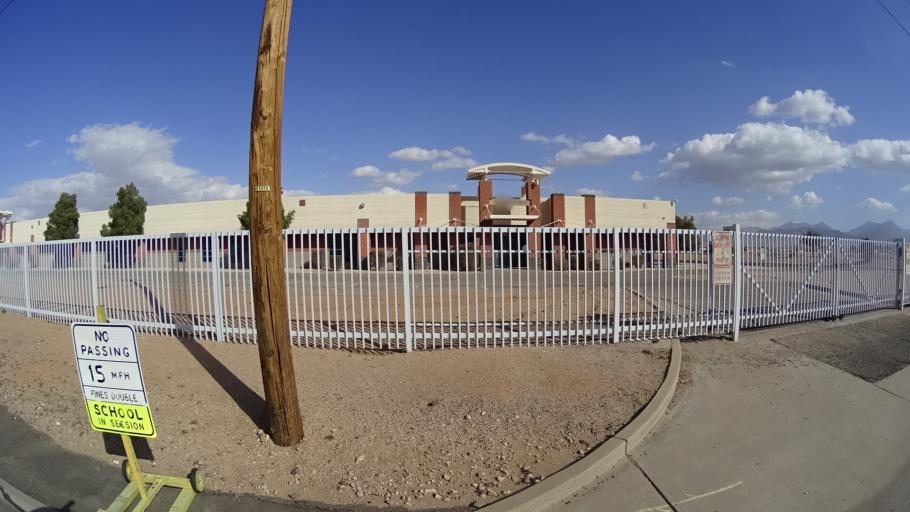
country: US
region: Arizona
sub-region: Mohave County
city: New Kingman-Butler
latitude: 35.2440
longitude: -114.0115
